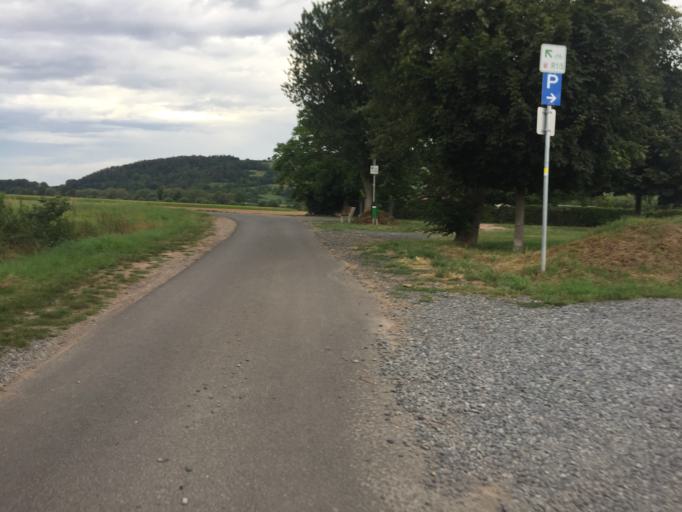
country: DE
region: Hesse
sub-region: Regierungsbezirk Kassel
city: Alheim
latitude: 51.0477
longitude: 9.6591
